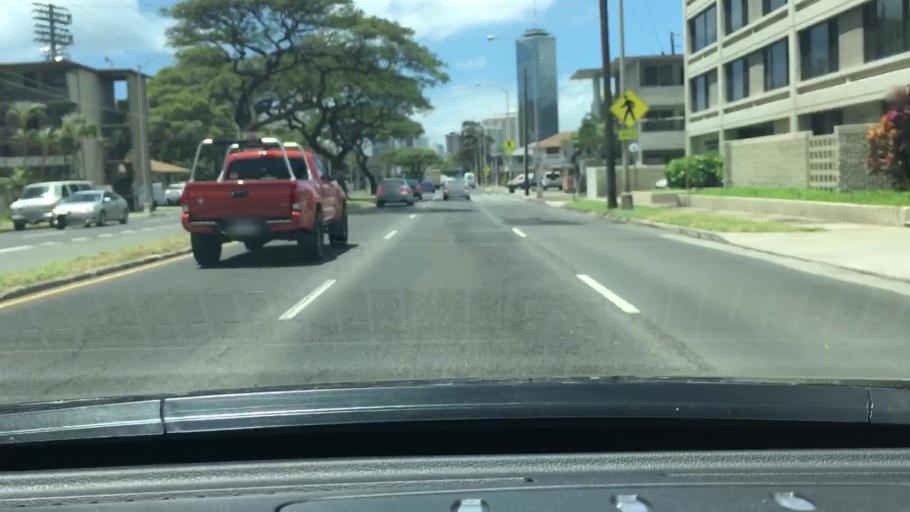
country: US
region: Hawaii
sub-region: Honolulu County
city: Honolulu
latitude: 21.2884
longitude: -157.8291
